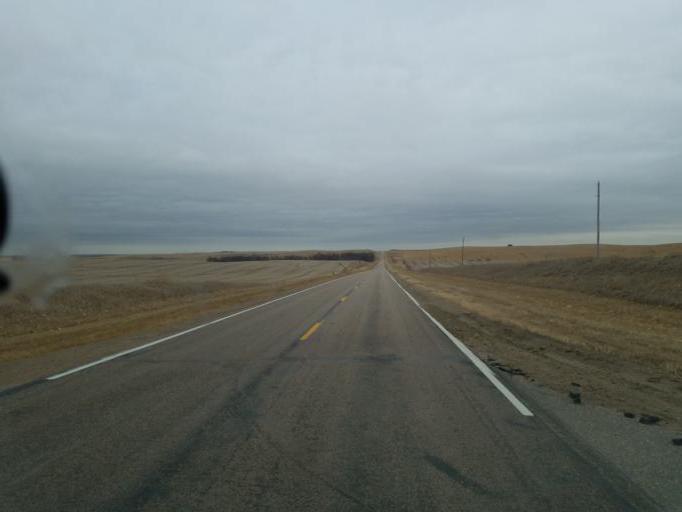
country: US
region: Nebraska
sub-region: Knox County
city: Bloomfield
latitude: 42.6127
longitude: -97.5051
